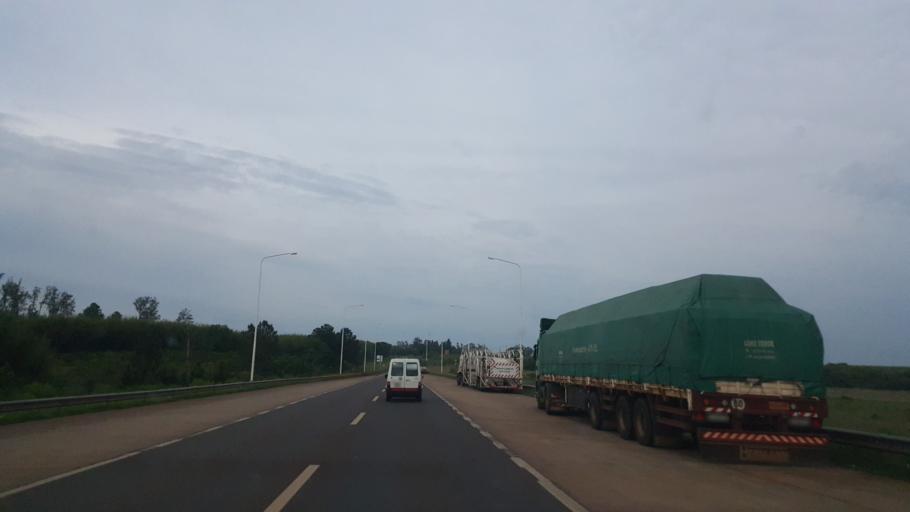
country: AR
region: Misiones
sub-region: Departamento de Apostoles
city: San Jose
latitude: -27.7837
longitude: -55.8215
